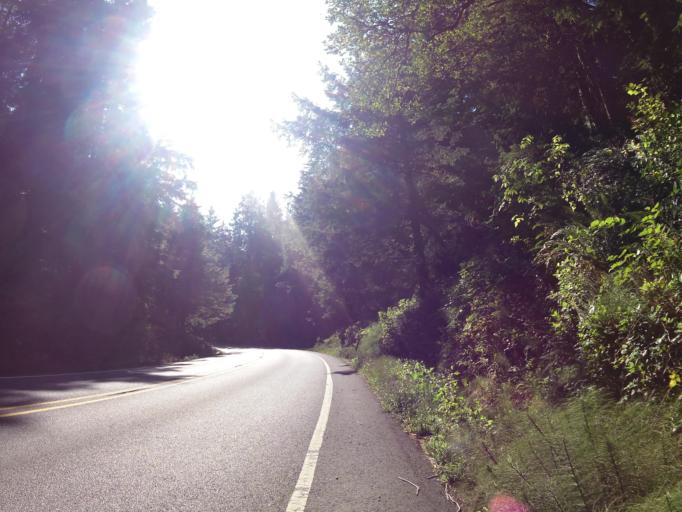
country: US
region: Oregon
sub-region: Clatsop County
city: Cannon Beach
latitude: 45.7560
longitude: -123.9619
